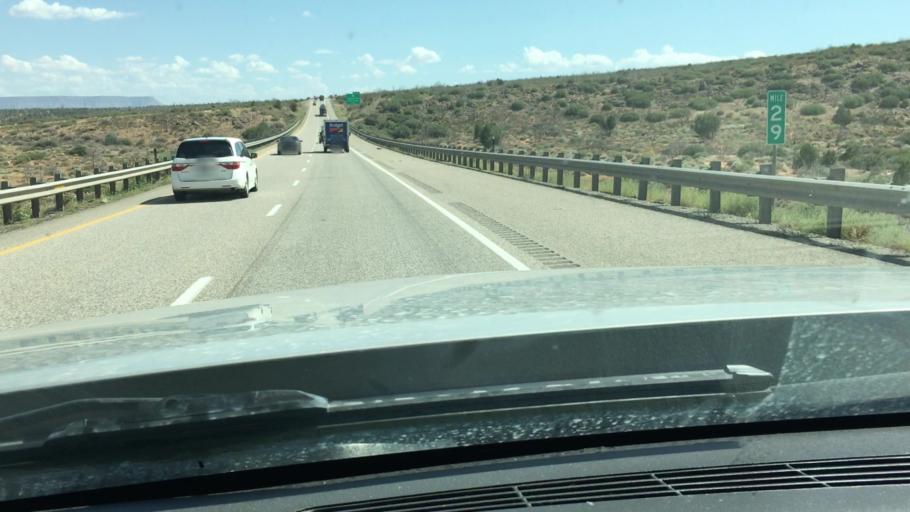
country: US
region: Utah
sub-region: Washington County
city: Toquerville
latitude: 37.3041
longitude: -113.2993
